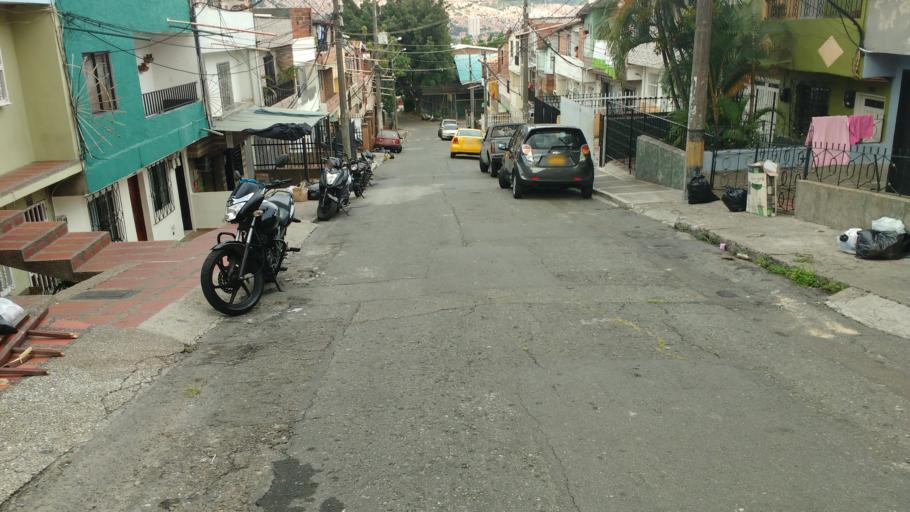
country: CO
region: Antioquia
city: Bello
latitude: 6.3008
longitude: -75.5750
